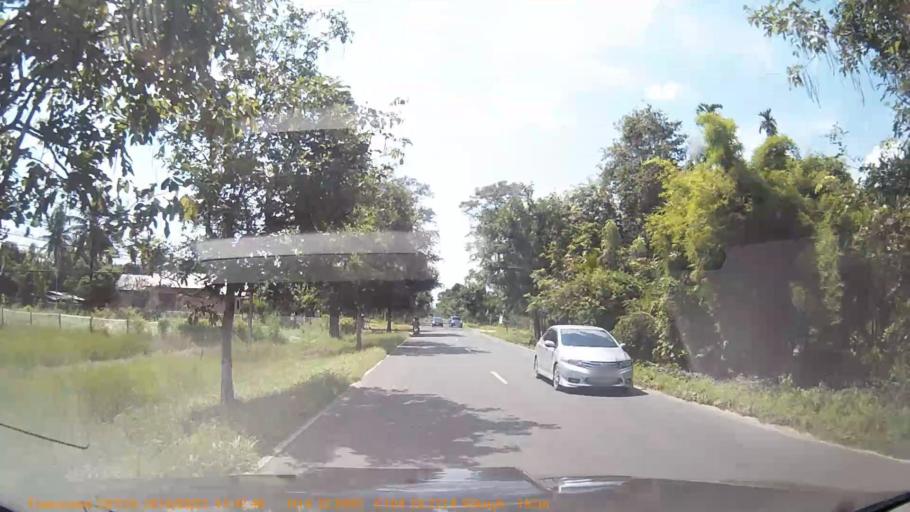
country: TH
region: Sisaket
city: Khun Han
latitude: 14.5452
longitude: 104.4698
